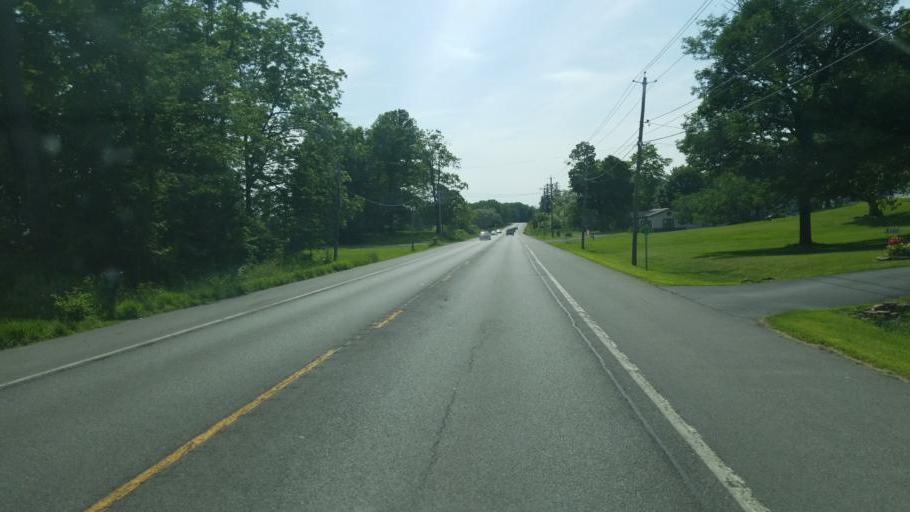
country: US
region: New York
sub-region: Ontario County
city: Holcomb
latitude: 42.9034
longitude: -77.5055
